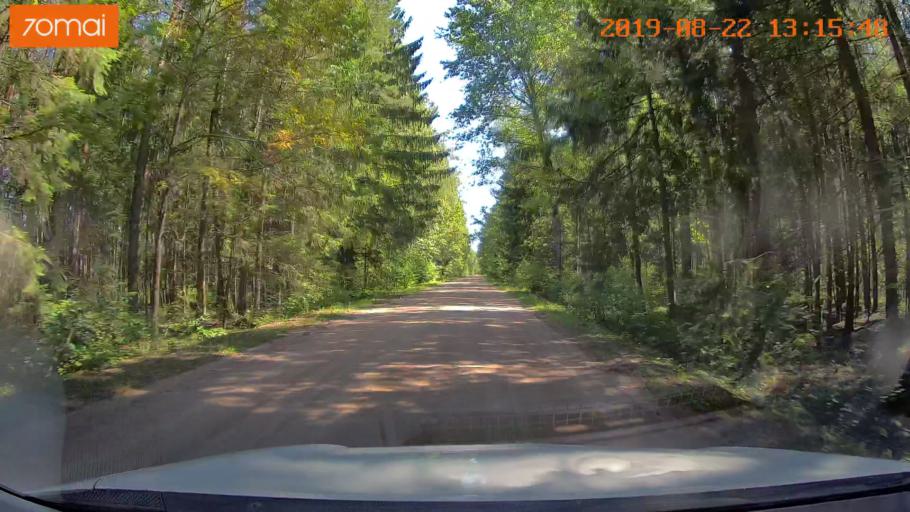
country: BY
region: Minsk
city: Prawdzinski
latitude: 53.2582
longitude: 27.9019
